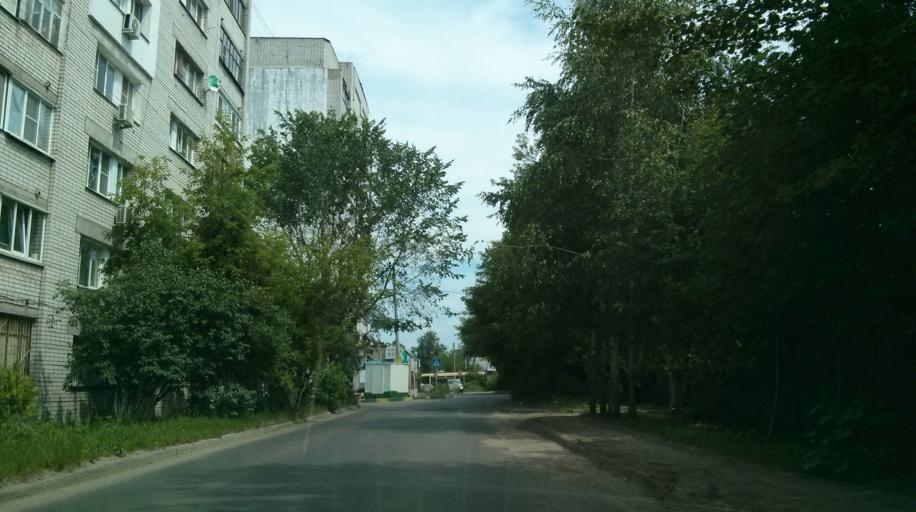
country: RU
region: Nizjnij Novgorod
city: Nizhniy Novgorod
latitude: 56.3004
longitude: 44.0260
